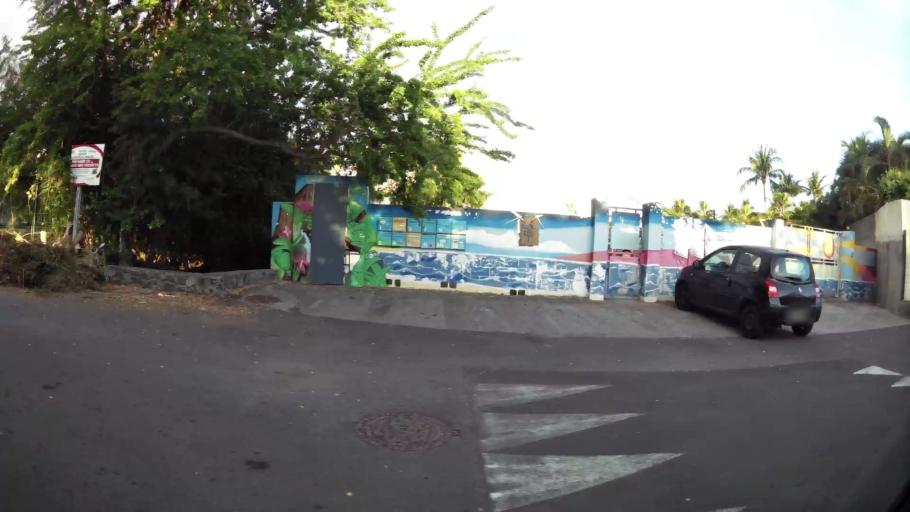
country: RE
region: Reunion
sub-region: Reunion
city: Saint-Paul
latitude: -21.0408
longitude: 55.2228
